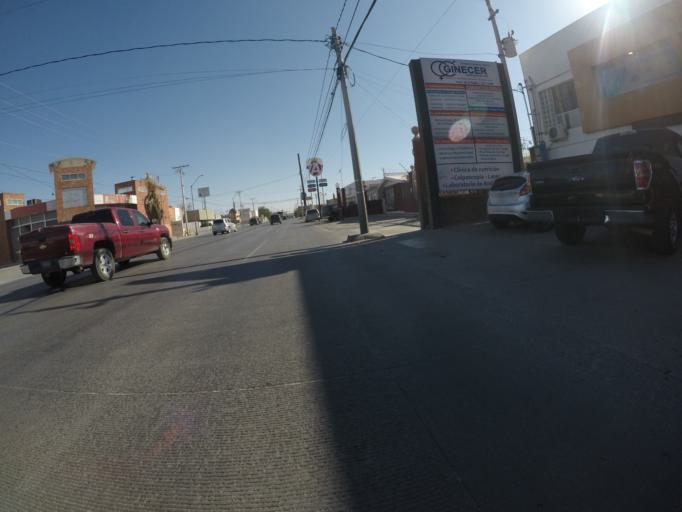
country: MX
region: Chihuahua
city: Ciudad Juarez
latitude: 31.7297
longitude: -106.4503
